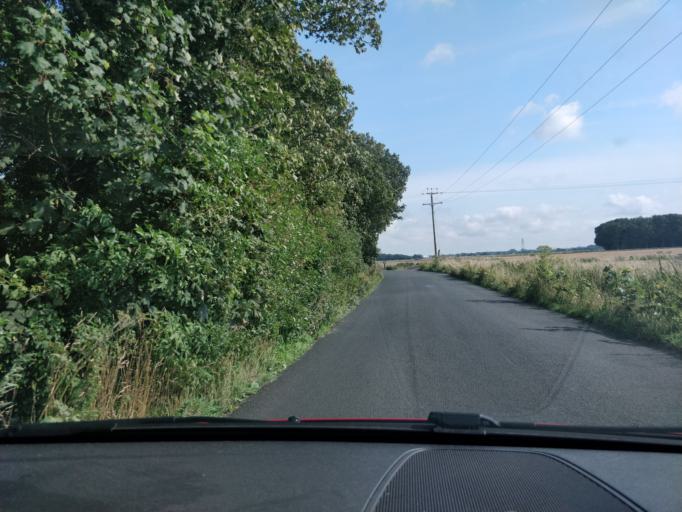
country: GB
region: England
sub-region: Lancashire
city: Banks
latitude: 53.6514
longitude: -2.9488
